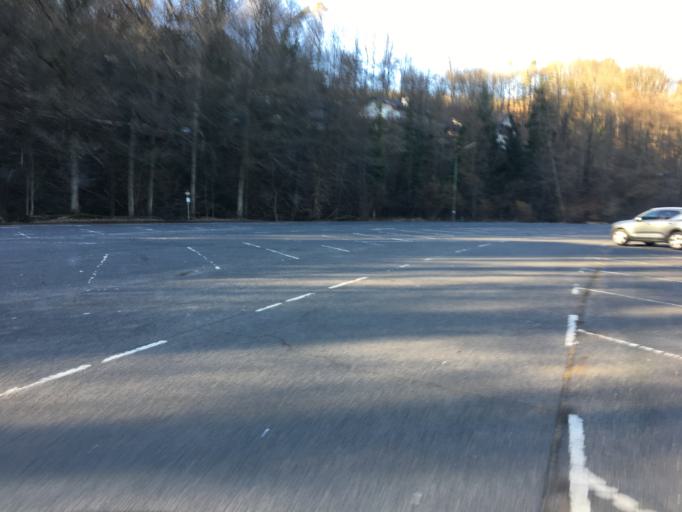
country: DE
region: North Rhine-Westphalia
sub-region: Regierungsbezirk Koln
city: Odenthal
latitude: 51.0582
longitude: 7.1331
